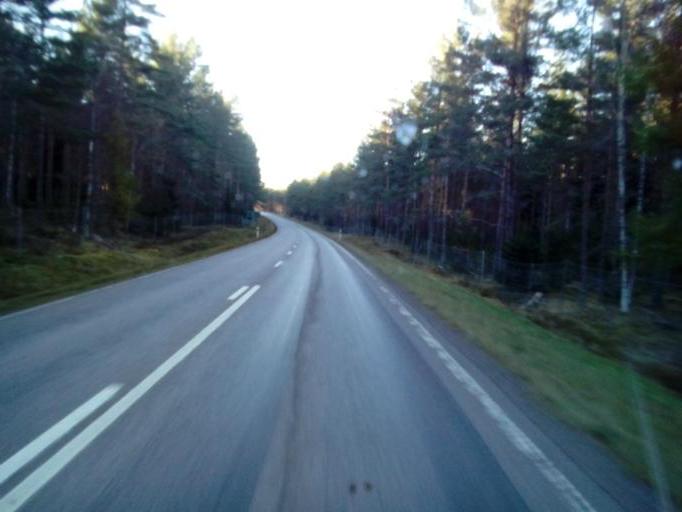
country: SE
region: OErebro
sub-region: Hallsbergs Kommun
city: Palsboda
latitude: 58.9380
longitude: 15.4276
